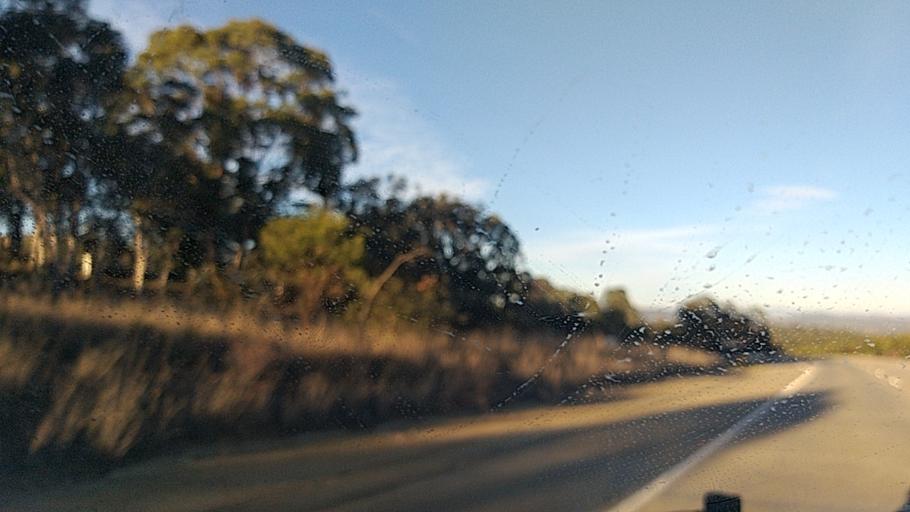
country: AU
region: New South Wales
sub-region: Yass Valley
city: Gundaroo
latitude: -35.1631
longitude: 149.3125
